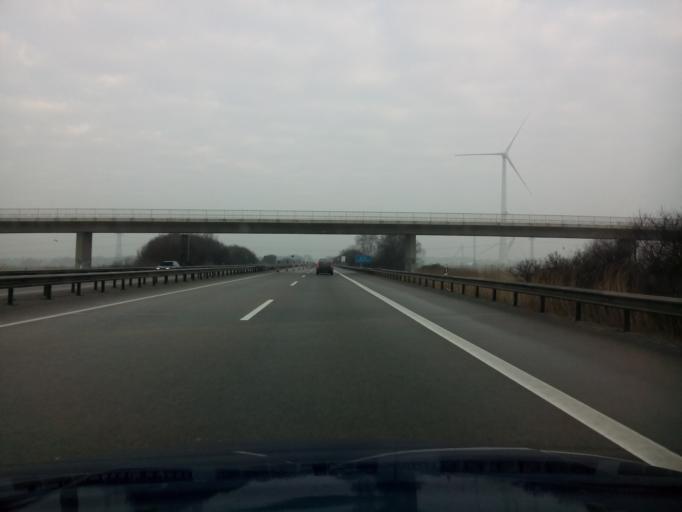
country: DE
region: Lower Saxony
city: Schiffdorf
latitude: 53.5555
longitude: 8.6196
